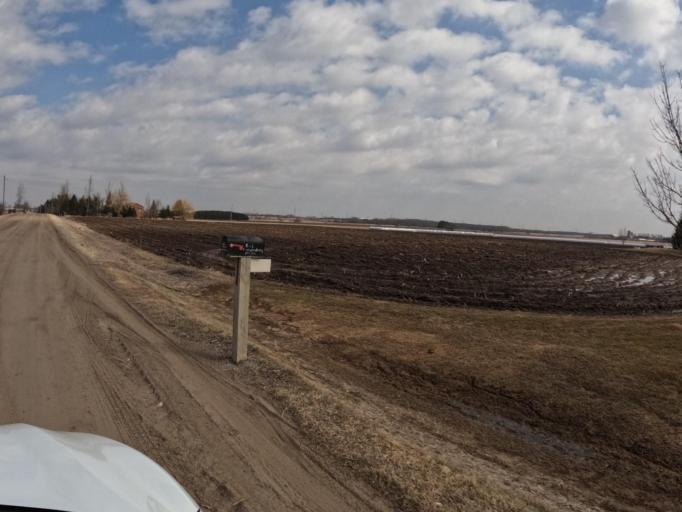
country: CA
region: Ontario
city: Orangeville
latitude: 43.9152
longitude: -80.2385
